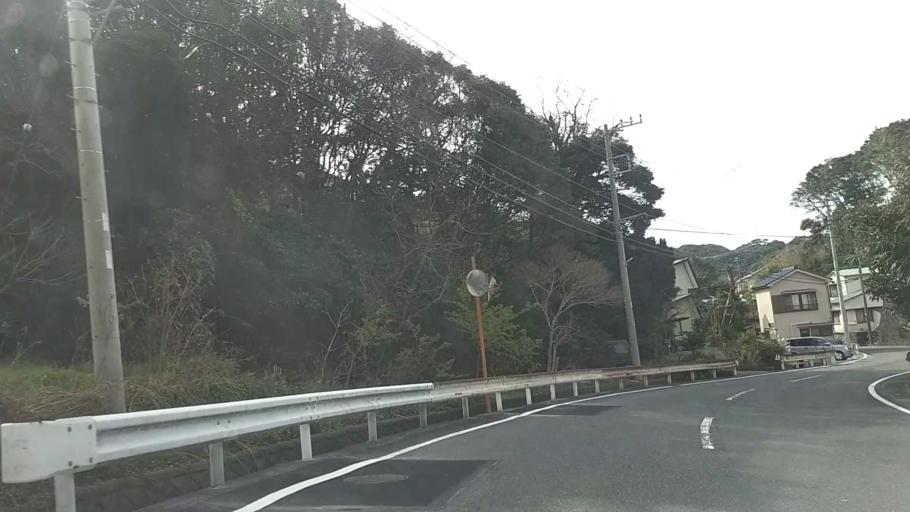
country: JP
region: Shizuoka
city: Shimoda
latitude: 34.6636
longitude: 138.9648
